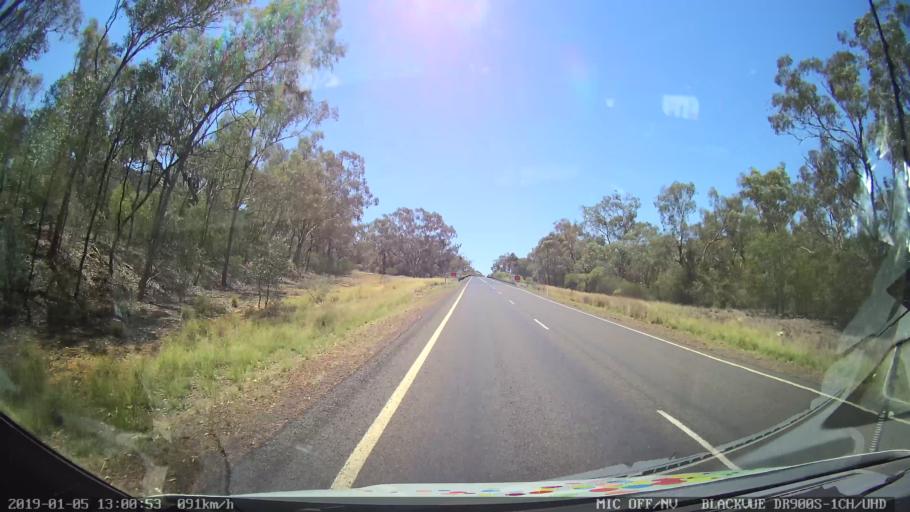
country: AU
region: New South Wales
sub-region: Narrabri
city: Boggabri
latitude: -31.1145
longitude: 149.7892
